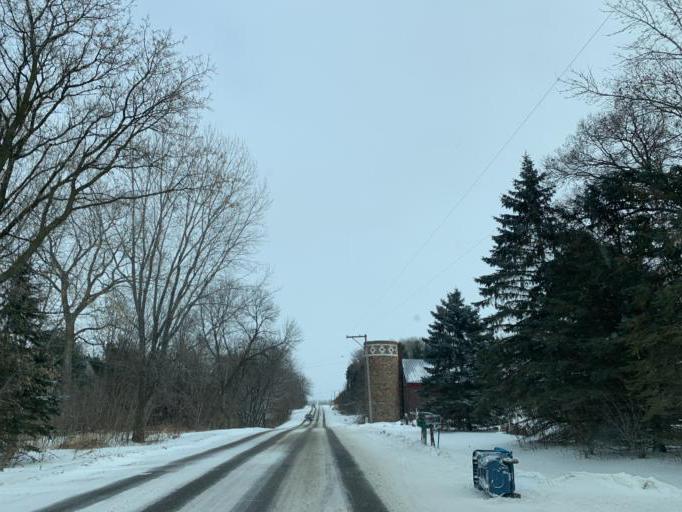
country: US
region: Minnesota
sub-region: Washington County
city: Cottage Grove
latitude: 44.8764
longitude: -92.9320
